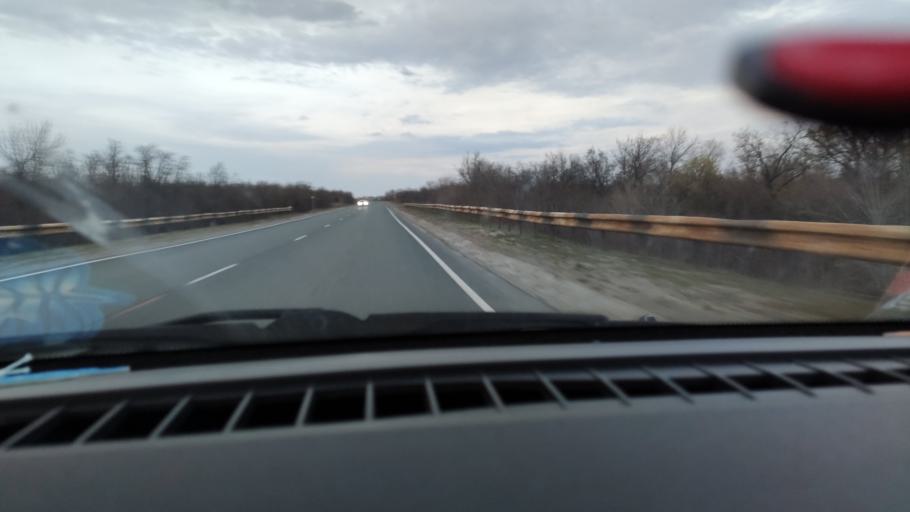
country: RU
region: Saratov
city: Sinodskoye
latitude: 51.9344
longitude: 46.5880
